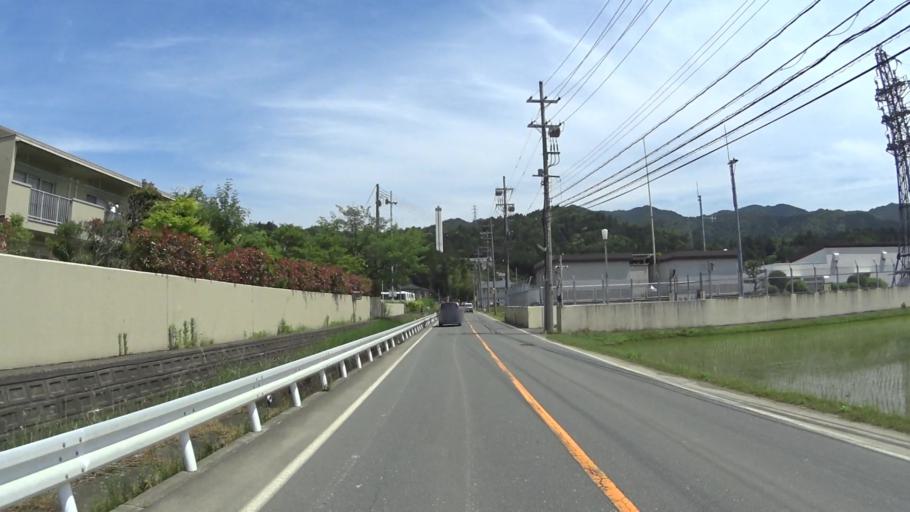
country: JP
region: Fukui
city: Obama
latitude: 35.4711
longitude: 135.6219
